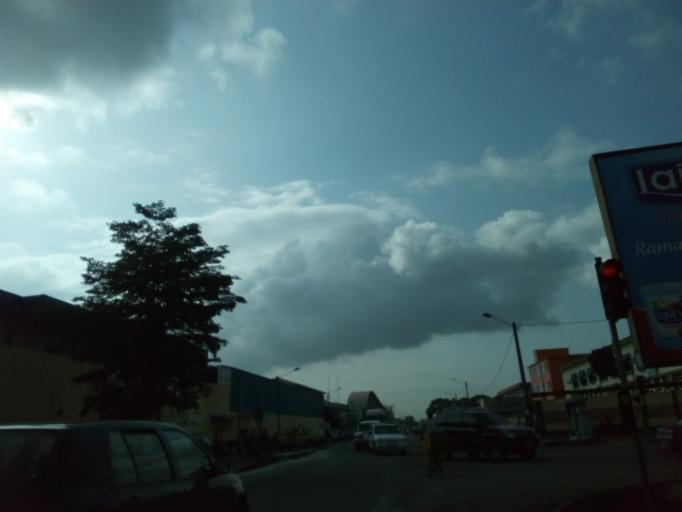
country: CI
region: Lagunes
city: Abidjan
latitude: 5.2938
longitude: -4.0007
